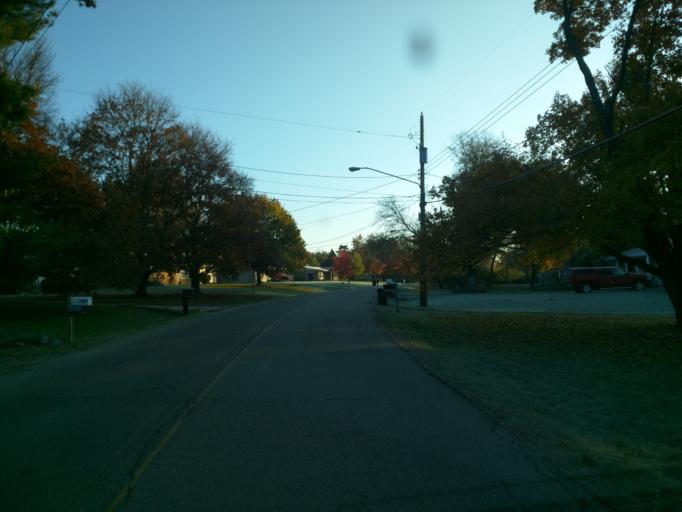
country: US
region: Michigan
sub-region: Ingham County
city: Edgemont Park
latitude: 42.7553
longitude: -84.6003
